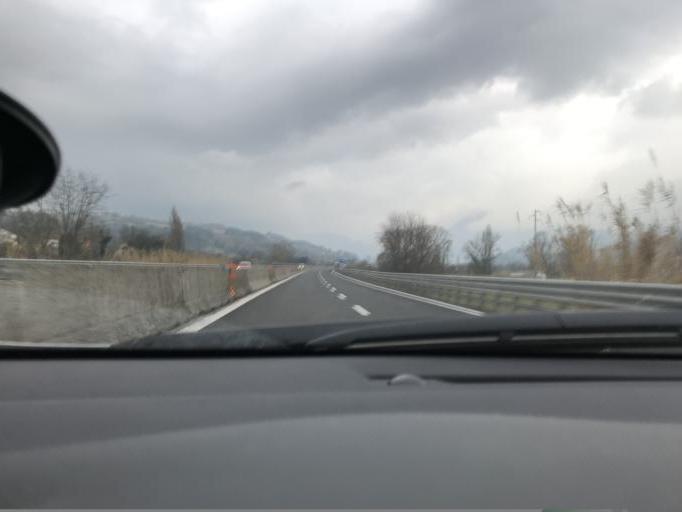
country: IT
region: The Marches
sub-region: Provincia di Ancona
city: Rosora
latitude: 43.4698
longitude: 13.0721
